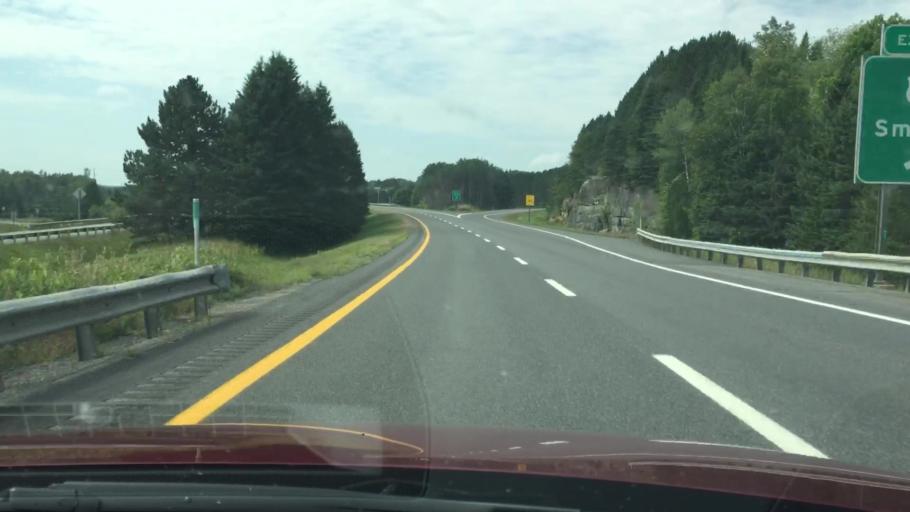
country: US
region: Maine
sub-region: Aroostook County
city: Hodgdon
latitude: 46.1454
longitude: -68.0551
